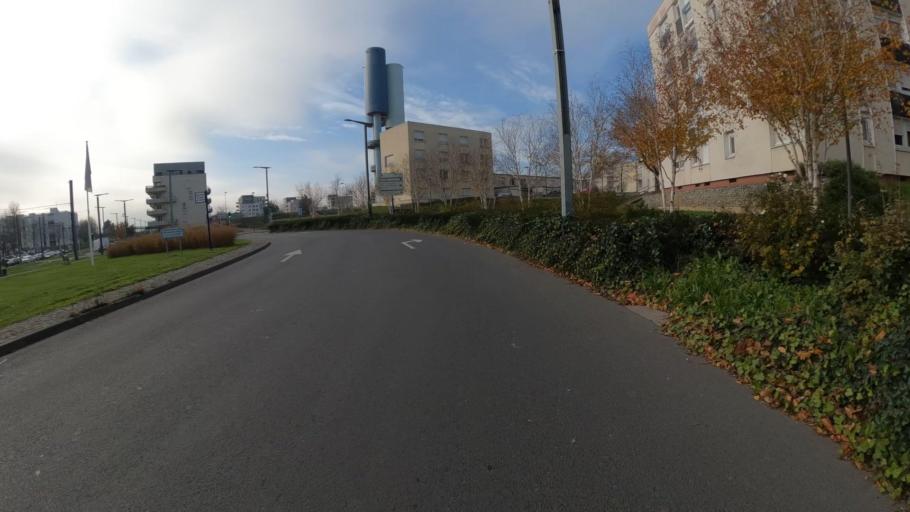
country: FR
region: Lower Normandy
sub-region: Departement du Calvados
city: Caen
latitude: 49.2031
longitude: -0.3407
